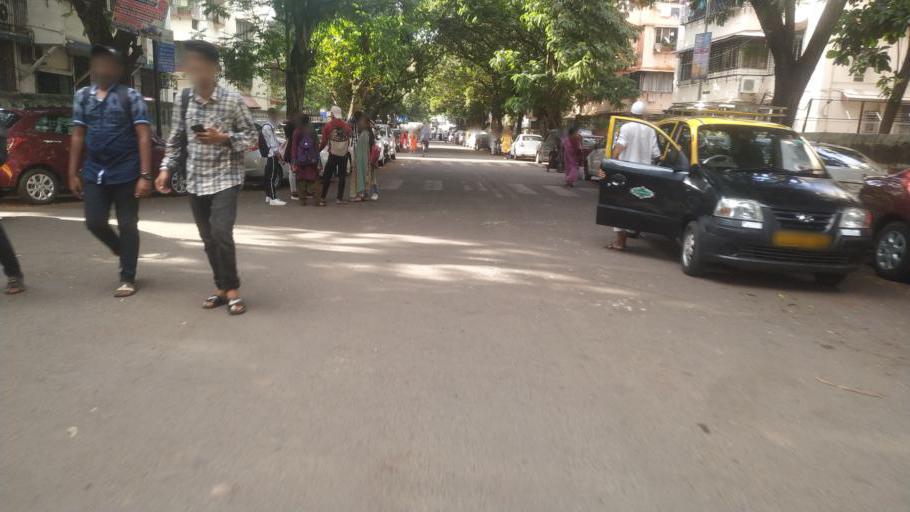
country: IN
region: Maharashtra
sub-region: Mumbai Suburban
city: Mumbai
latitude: 19.0216
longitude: 72.8598
